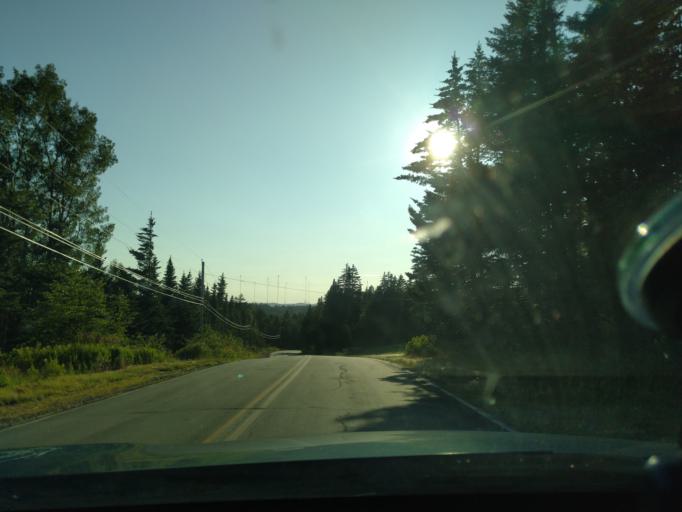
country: US
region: Maine
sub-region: Washington County
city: Machiasport
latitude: 44.6596
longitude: -67.2196
